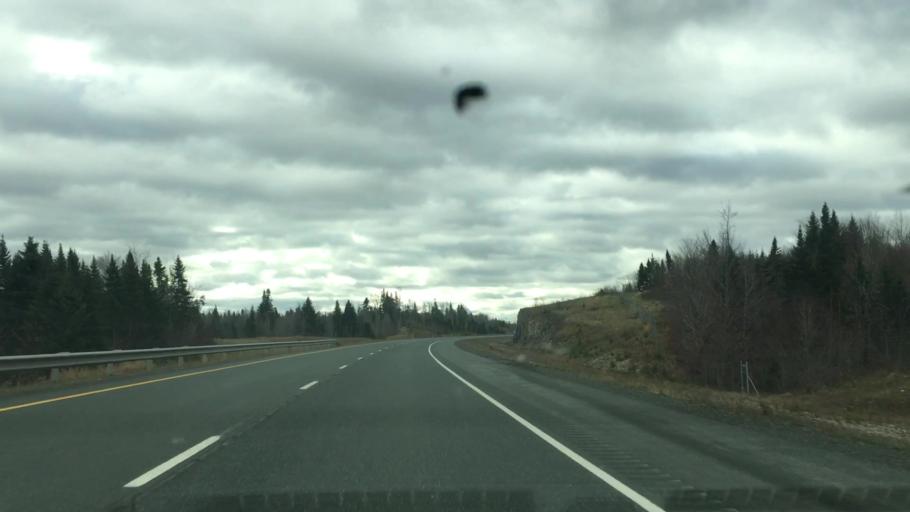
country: US
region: Maine
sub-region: Aroostook County
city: Easton
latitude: 46.6191
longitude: -67.7387
